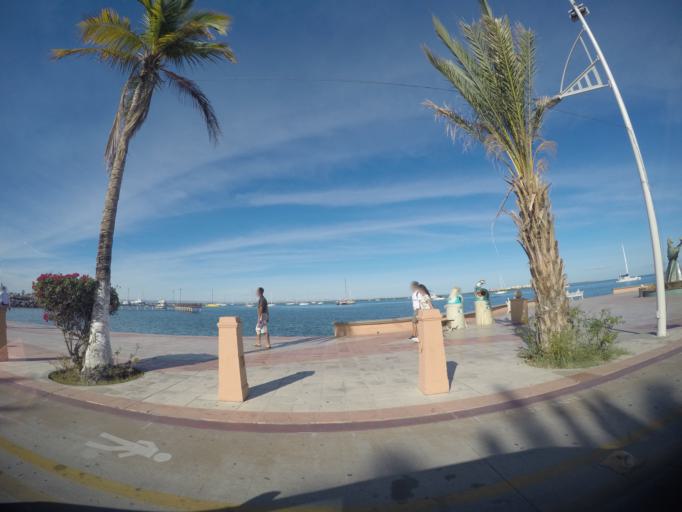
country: MX
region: Baja California Sur
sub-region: La Paz
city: La Paz
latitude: 24.1941
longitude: -110.2959
